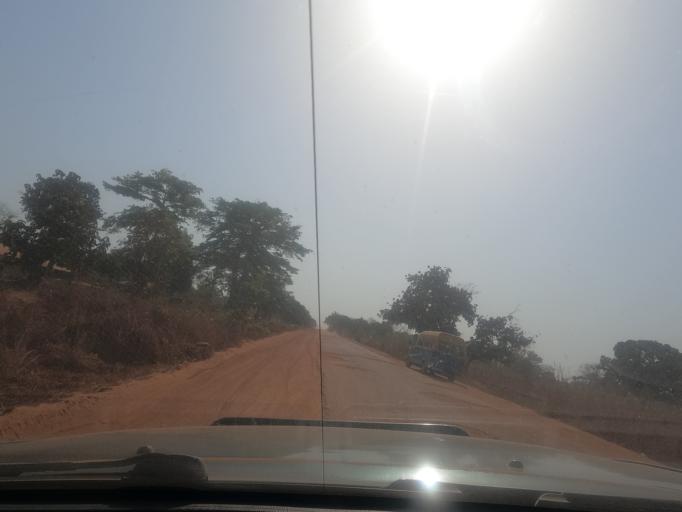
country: GW
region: Oio
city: Mansoa
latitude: 12.0054
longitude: -15.4219
